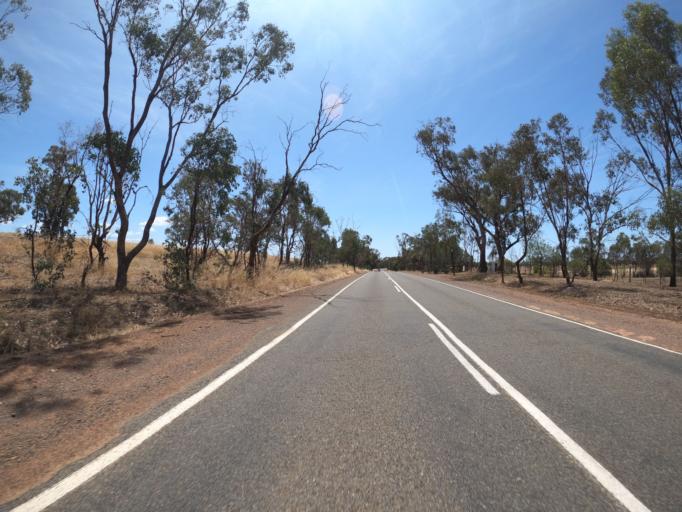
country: AU
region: Victoria
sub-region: Benalla
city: Benalla
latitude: -36.3223
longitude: 145.9586
